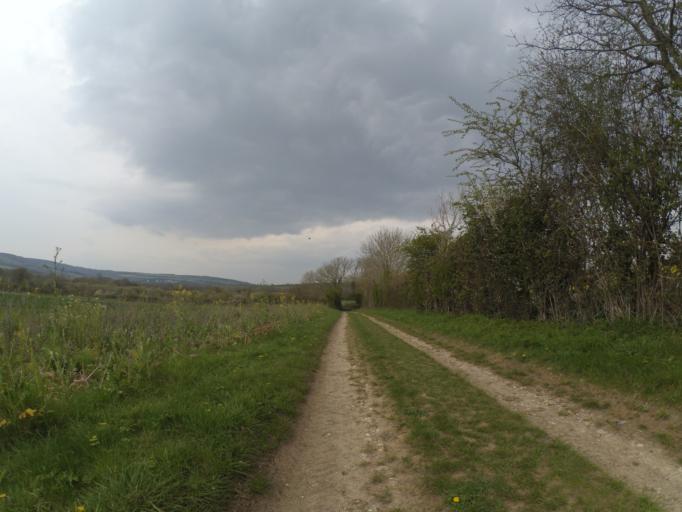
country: GB
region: England
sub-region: West Sussex
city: Arundel
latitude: 50.8780
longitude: -0.5303
